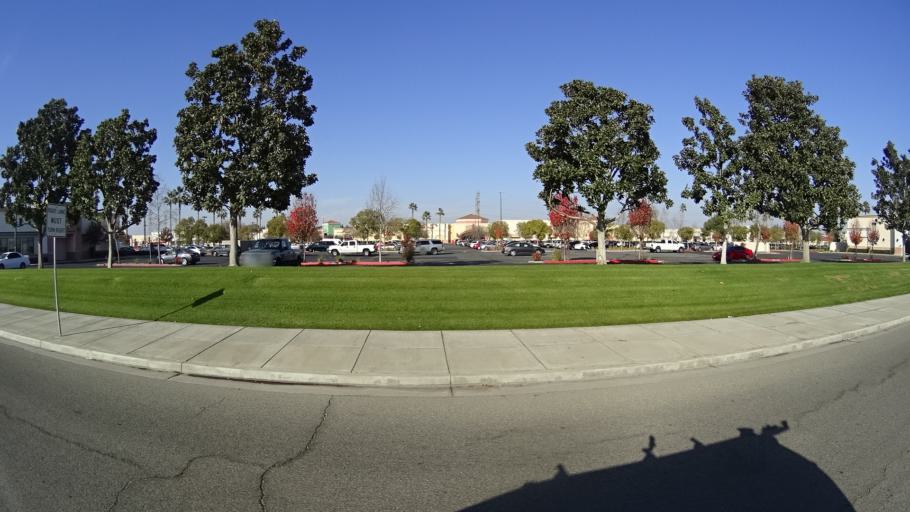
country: US
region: California
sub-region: Kern County
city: Greenacres
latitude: 35.3835
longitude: -119.1035
